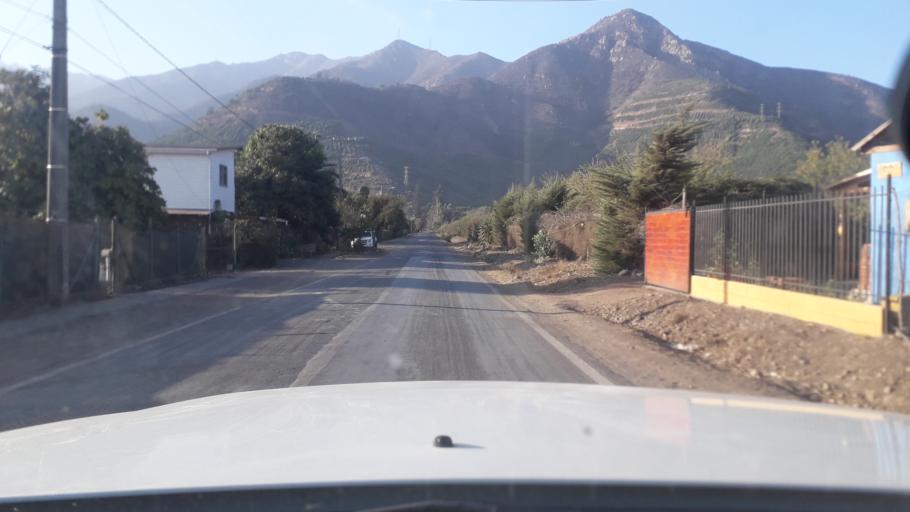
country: CL
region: Valparaiso
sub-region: Provincia de San Felipe
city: Llaillay
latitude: -32.8252
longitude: -71.0299
